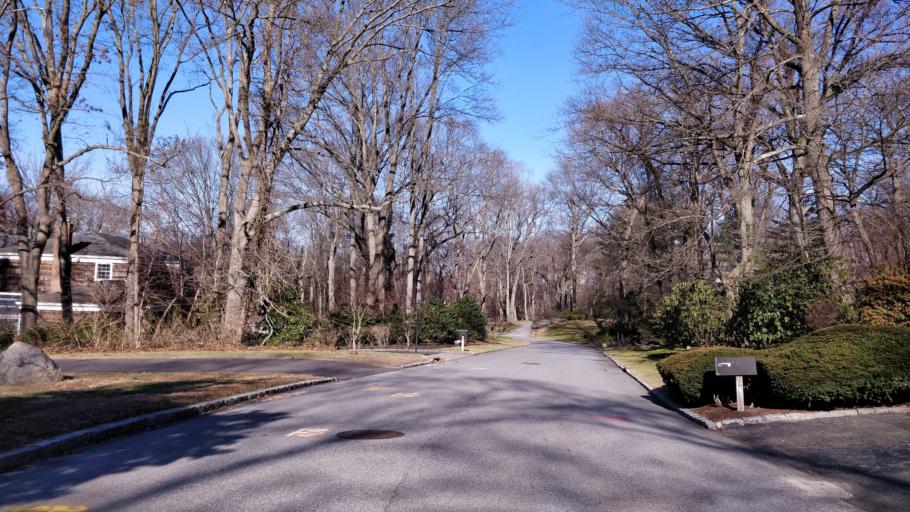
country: US
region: New York
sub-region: Nassau County
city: Brookville
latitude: 40.8118
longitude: -73.5795
